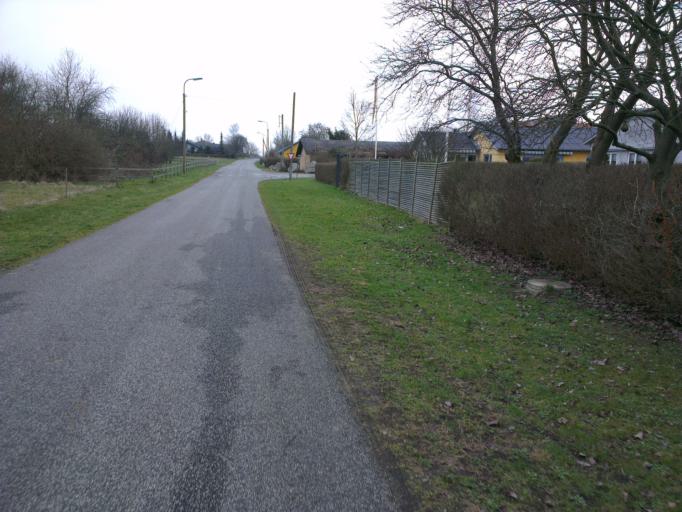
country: DK
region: Capital Region
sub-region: Frederikssund Kommune
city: Skibby
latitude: 55.7469
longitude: 11.9509
